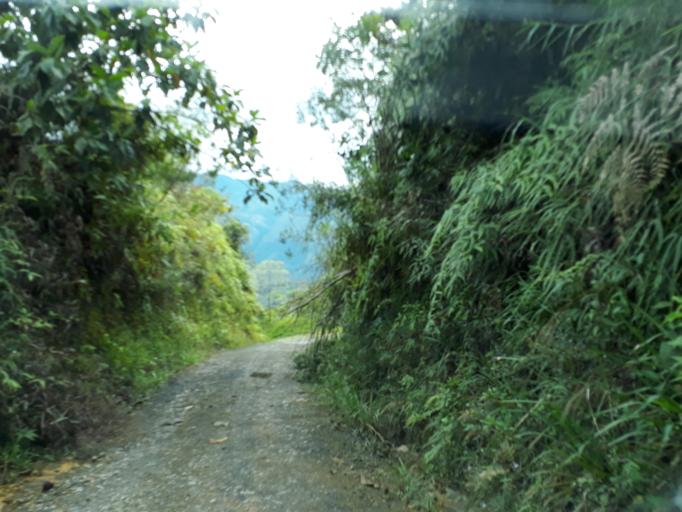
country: CO
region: Boyaca
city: Quipama
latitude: 5.3948
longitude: -74.1207
